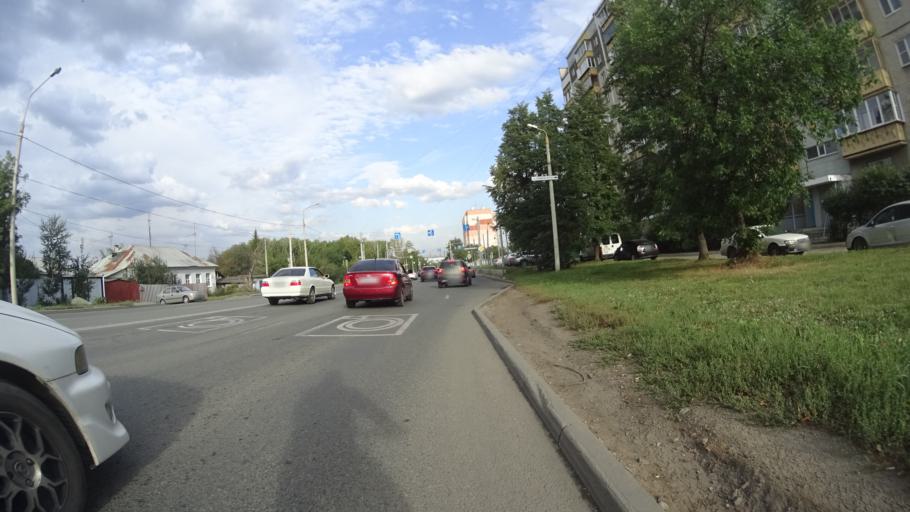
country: RU
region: Chelyabinsk
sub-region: Gorod Chelyabinsk
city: Chelyabinsk
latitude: 55.1984
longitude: 61.3609
